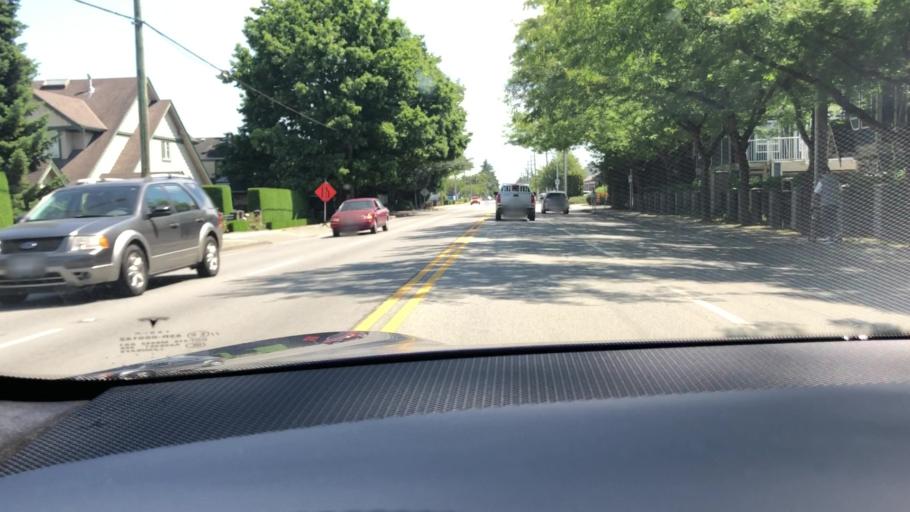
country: CA
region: British Columbia
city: Richmond
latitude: 49.1845
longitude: -123.0958
